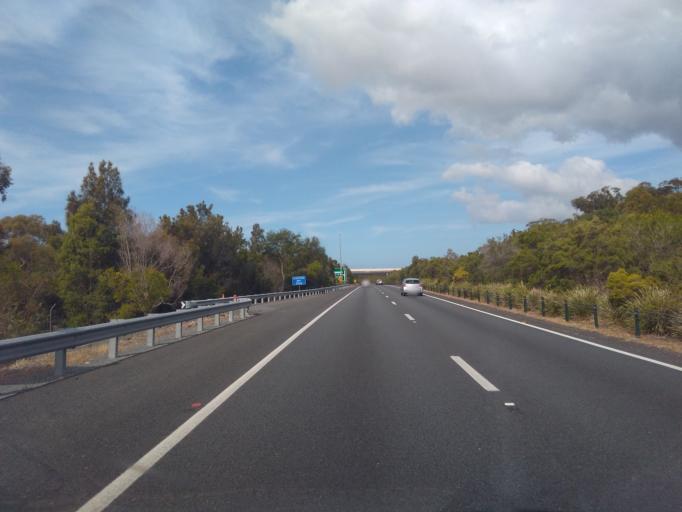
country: AU
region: Queensland
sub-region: Gold Coast
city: Tugun
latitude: -28.1654
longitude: 153.5002
